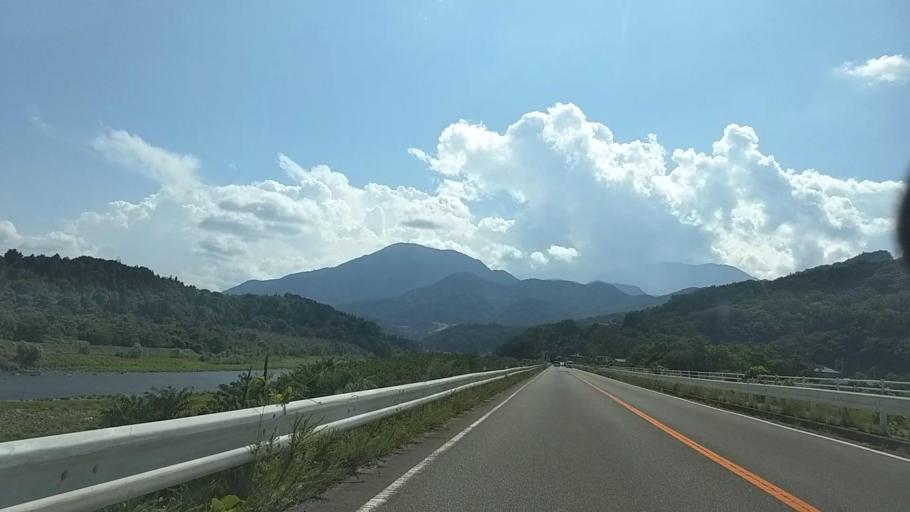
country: JP
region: Yamanashi
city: Ryuo
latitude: 35.4496
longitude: 138.4444
